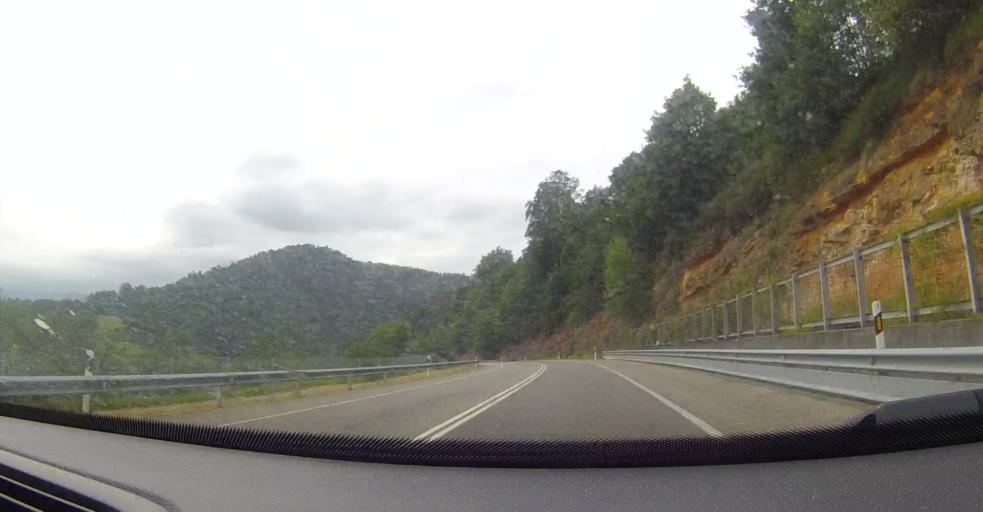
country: ES
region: Asturias
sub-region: Province of Asturias
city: Pilona
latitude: 43.3533
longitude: -5.3685
